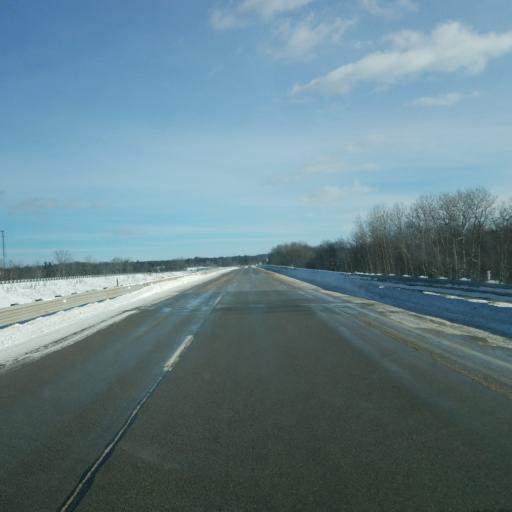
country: US
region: Michigan
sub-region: Clare County
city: Clare
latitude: 43.8668
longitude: -84.9018
